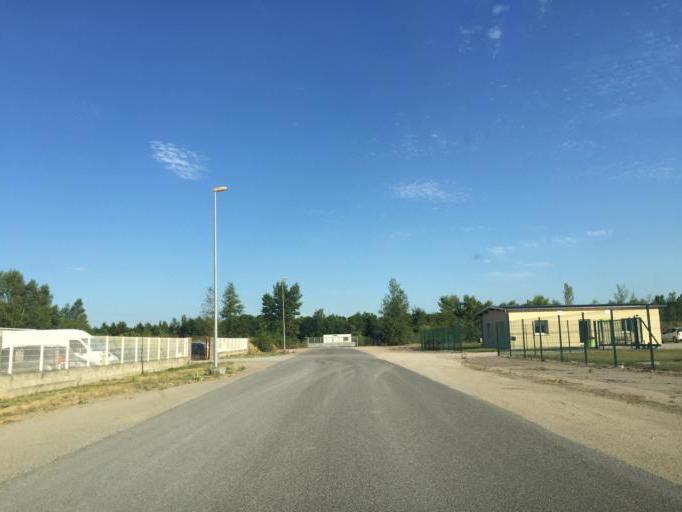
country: FR
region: Auvergne
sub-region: Departement de l'Allier
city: Toulon-sur-Allier
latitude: 46.5372
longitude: 3.3703
